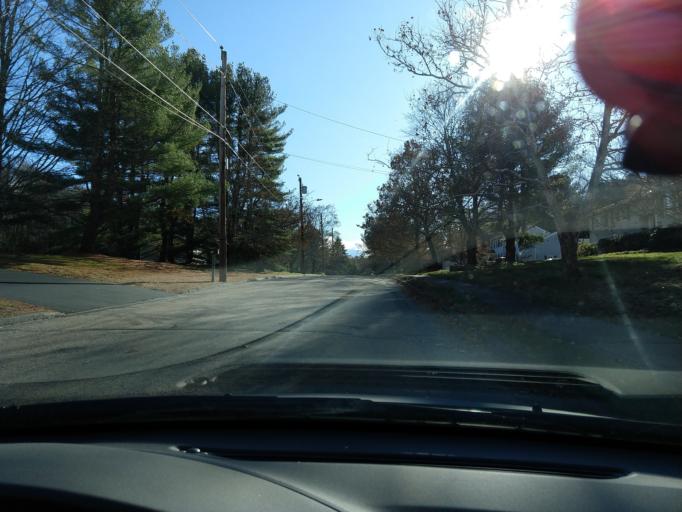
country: US
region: Massachusetts
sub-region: Middlesex County
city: Pinehurst
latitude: 42.4995
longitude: -71.2428
